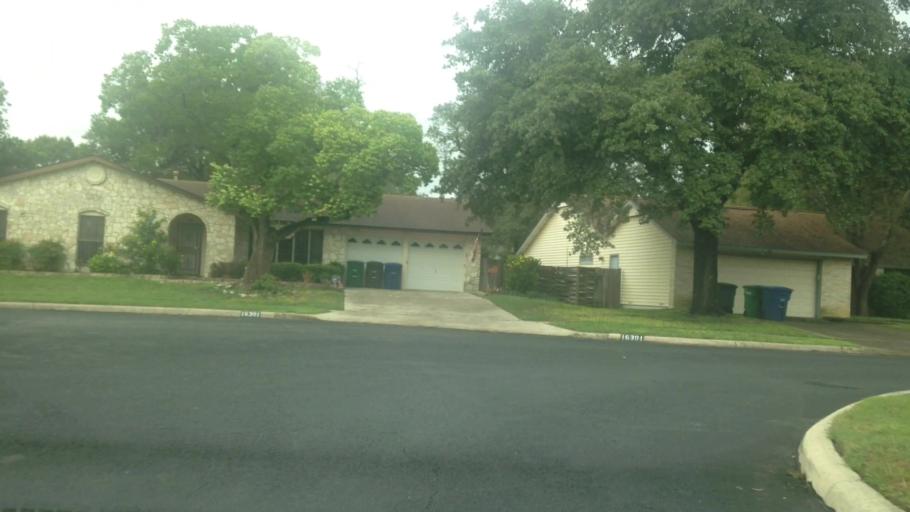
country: US
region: Texas
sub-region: Bexar County
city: Live Oak
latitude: 29.5895
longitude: -98.3740
